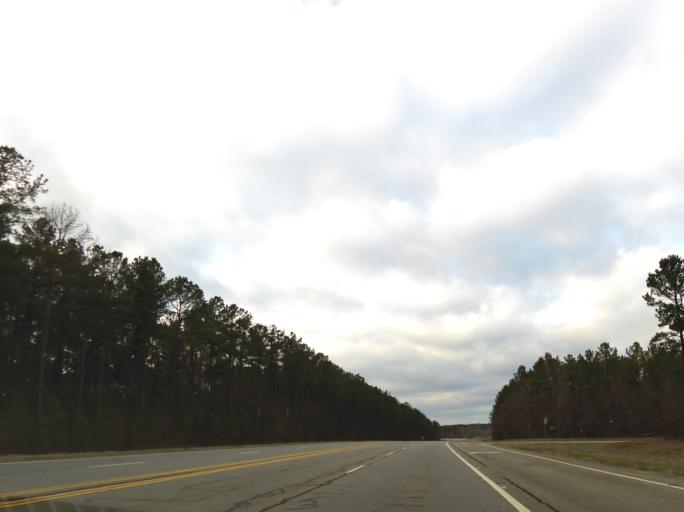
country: US
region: Georgia
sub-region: Bleckley County
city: Cochran
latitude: 32.4937
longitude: -83.4014
